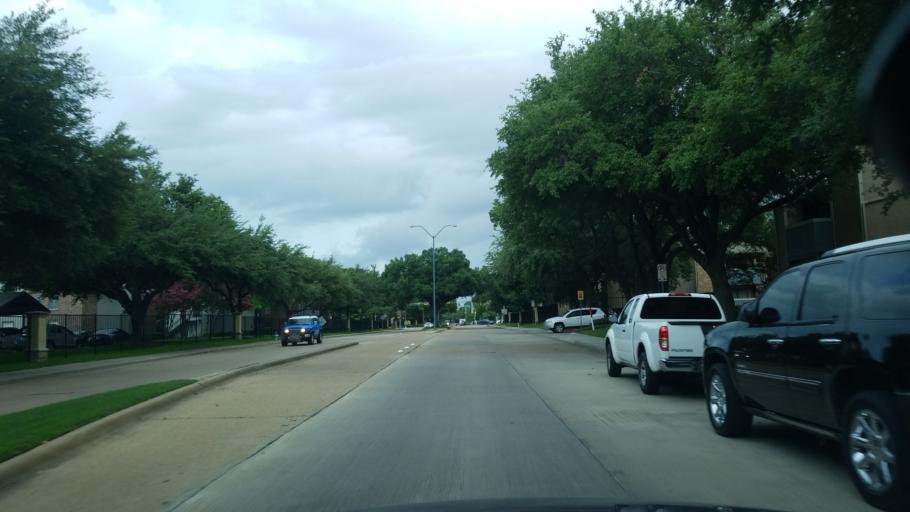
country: US
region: Texas
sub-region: Dallas County
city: Highland Park
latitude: 32.8527
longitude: -96.7645
